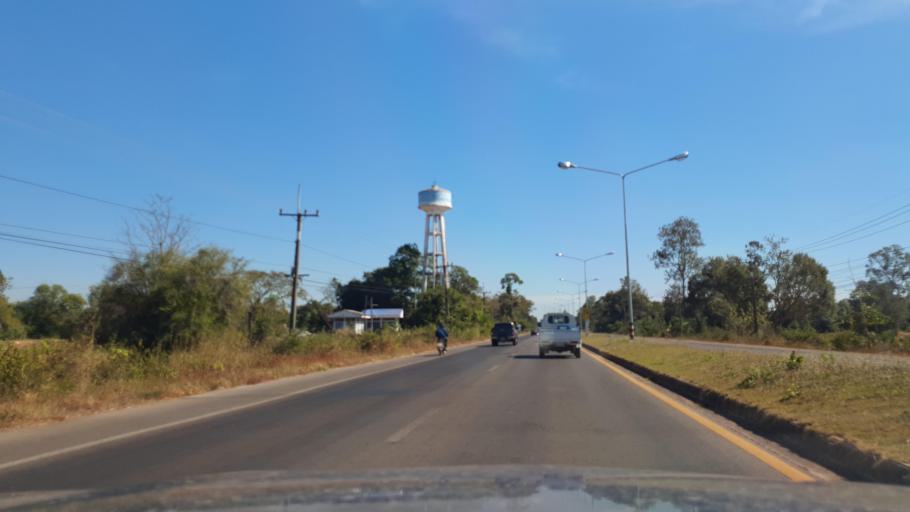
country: TH
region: Sakon Nakhon
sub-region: Amphoe Khok Si Suphan
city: Khok Si Suphan
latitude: 17.0745
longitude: 104.2066
